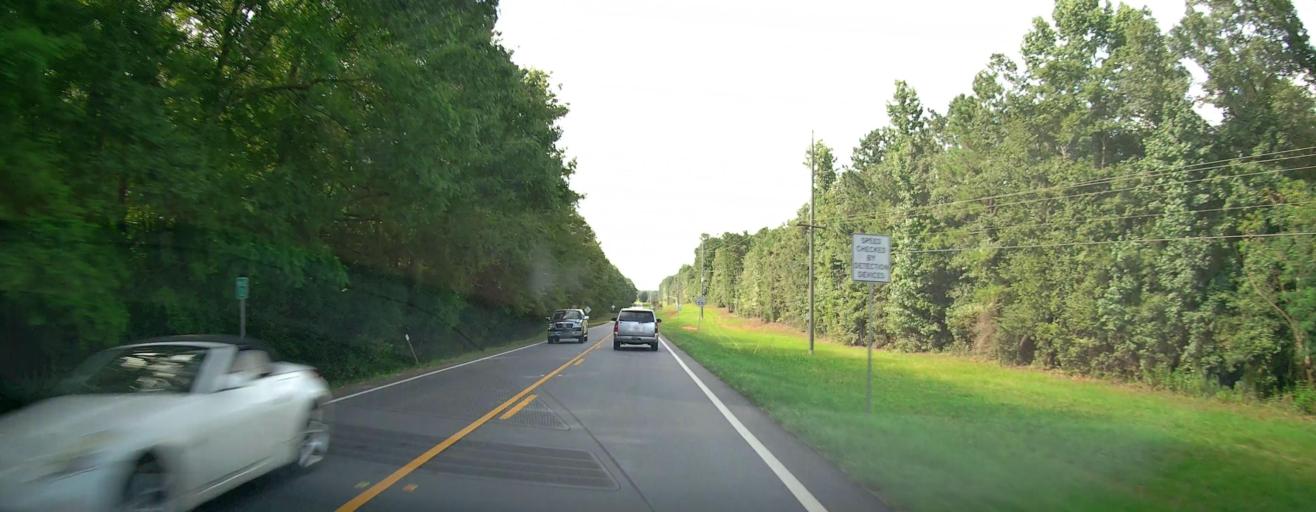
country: US
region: Georgia
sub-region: Upson County
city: Hannahs Mill
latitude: 32.9837
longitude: -84.5000
